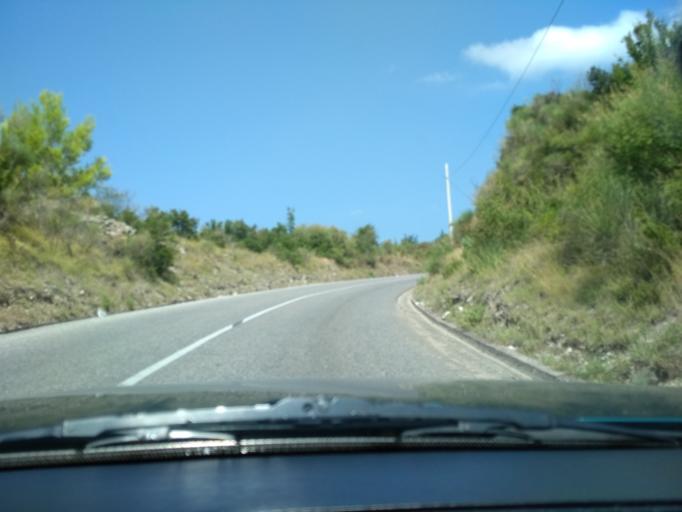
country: ME
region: Kotor
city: Kotor
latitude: 42.3869
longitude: 18.7574
